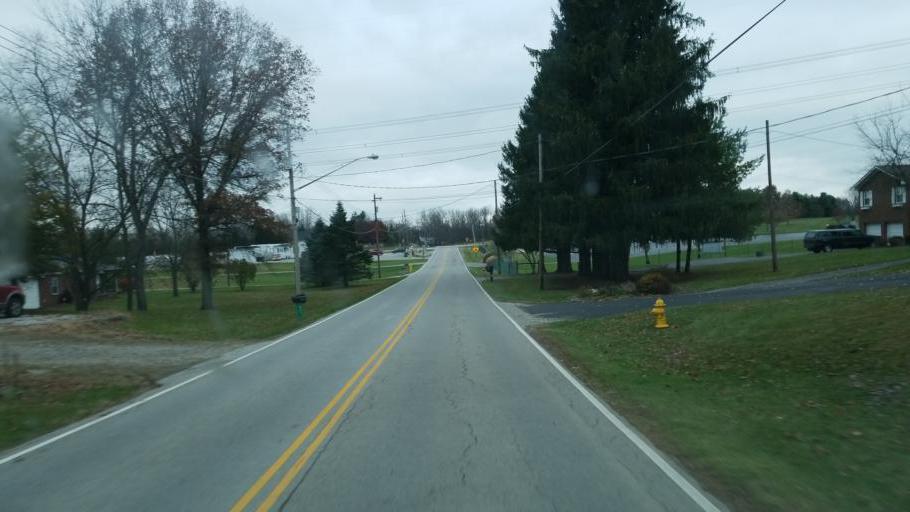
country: US
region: Ohio
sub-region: Delaware County
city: Sunbury
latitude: 40.2264
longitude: -82.8829
